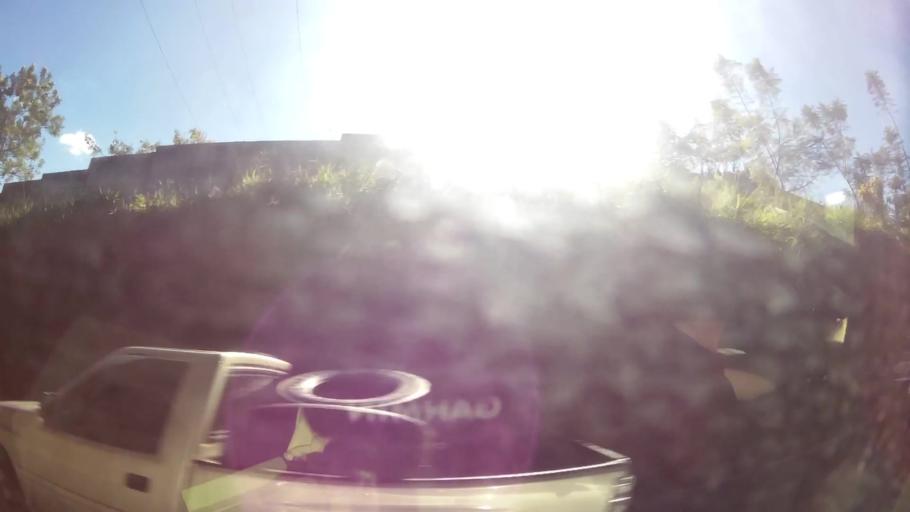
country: GT
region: Guatemala
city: Villa Nueva
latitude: 14.5398
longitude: -90.6091
